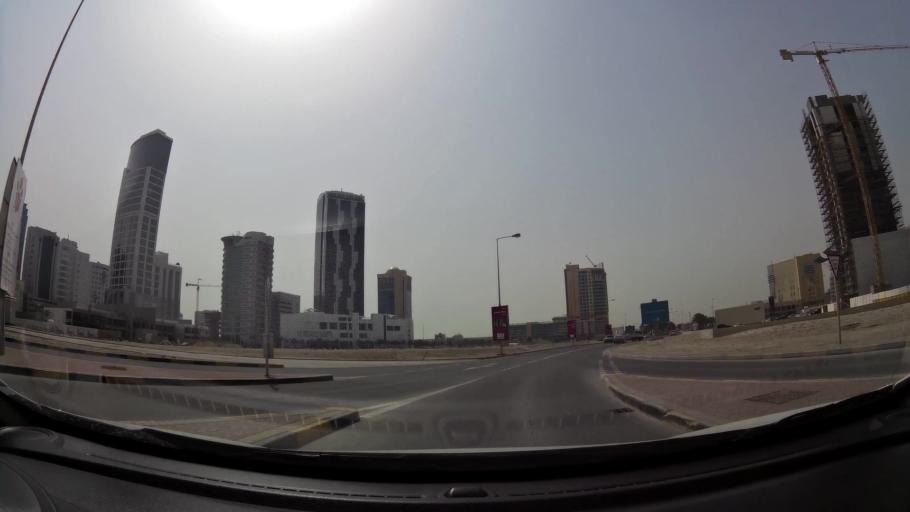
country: BH
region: Manama
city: Jidd Hafs
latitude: 26.2377
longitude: 50.5347
